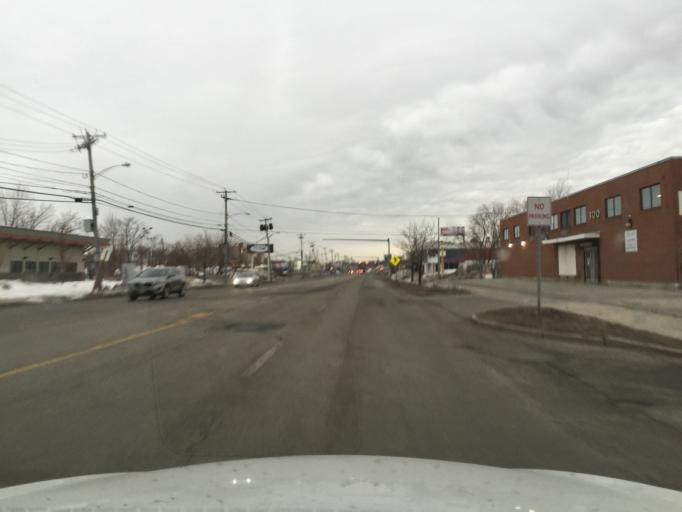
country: US
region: Massachusetts
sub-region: Middlesex County
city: Medford
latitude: 42.4043
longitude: -71.1001
